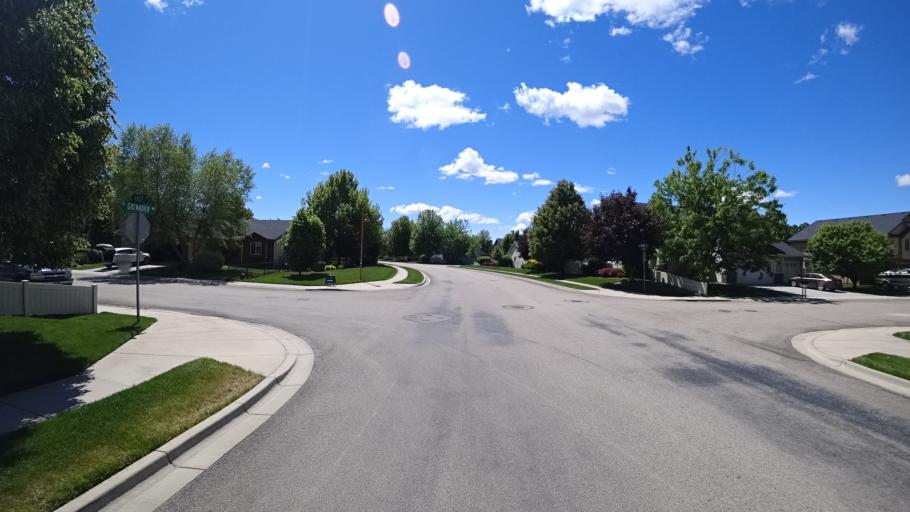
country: US
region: Idaho
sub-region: Ada County
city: Meridian
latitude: 43.6319
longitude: -116.3429
